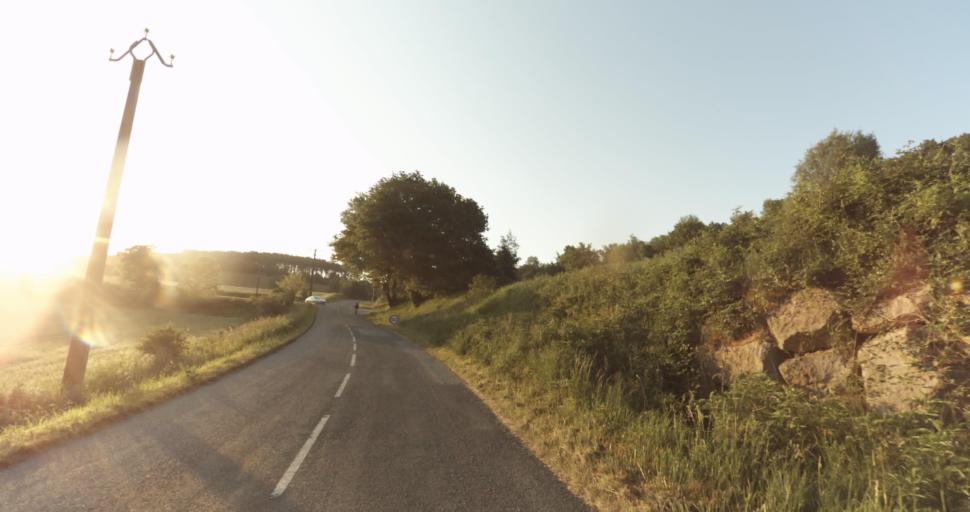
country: FR
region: Midi-Pyrenees
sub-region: Departement du Gers
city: Pujaudran
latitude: 43.6228
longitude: 1.1684
